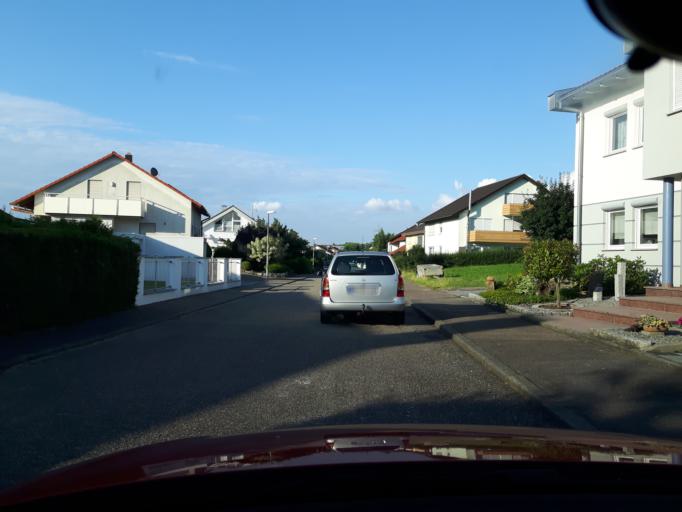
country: DE
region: Baden-Wuerttemberg
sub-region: Regierungsbezirk Stuttgart
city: Pfaffenhofen
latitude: 49.1091
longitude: 8.9854
